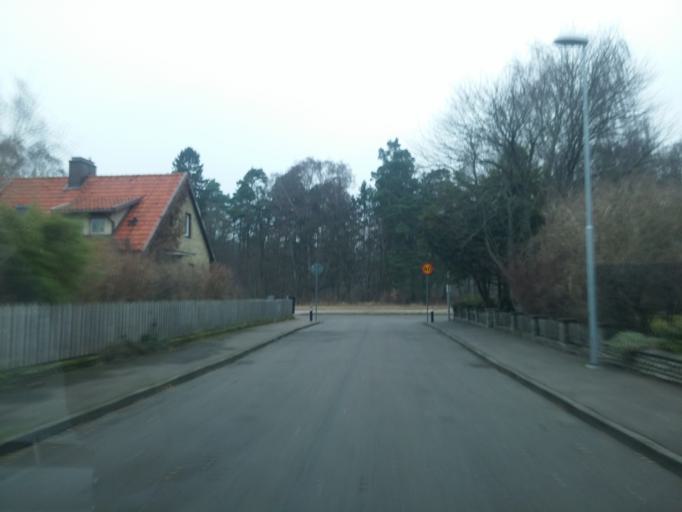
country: SE
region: Skane
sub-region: Angelholms Kommun
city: AEngelholm
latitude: 56.2366
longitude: 12.8490
